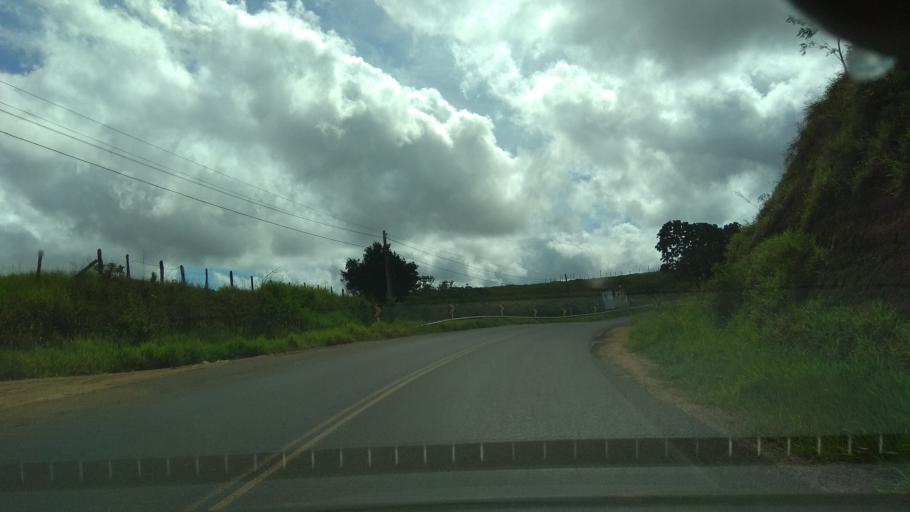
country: BR
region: Bahia
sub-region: Mutuipe
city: Mutuipe
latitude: -13.1666
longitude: -39.4108
